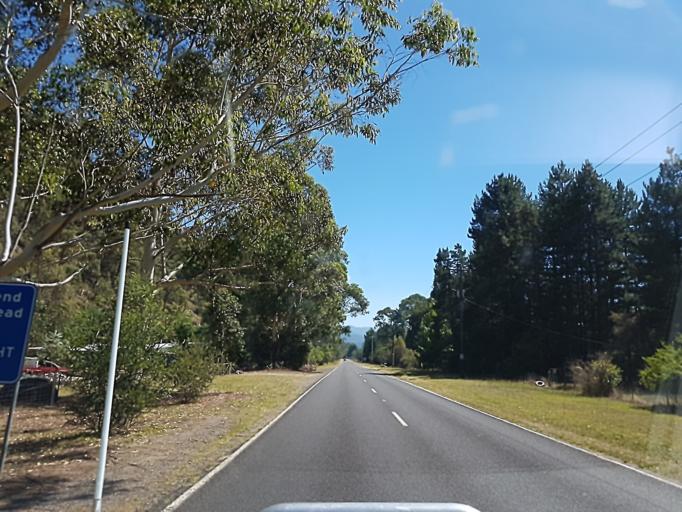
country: AU
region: Victoria
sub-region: Alpine
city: Mount Beauty
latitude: -36.7780
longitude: 147.0330
